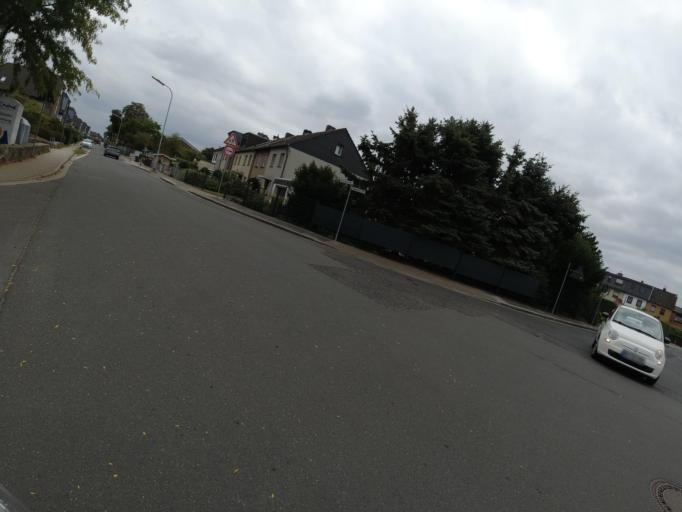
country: DE
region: North Rhine-Westphalia
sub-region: Regierungsbezirk Dusseldorf
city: Moers
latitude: 51.4614
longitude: 6.6629
